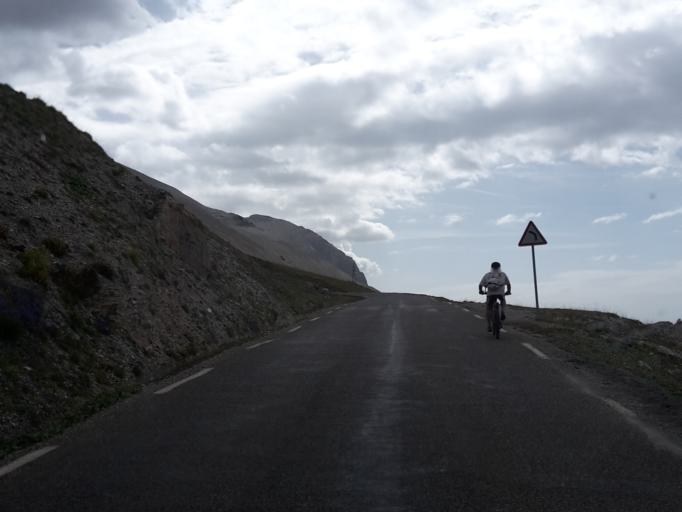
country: FR
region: Rhone-Alpes
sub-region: Departement de la Savoie
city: Valloire
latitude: 45.0608
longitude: 6.4103
